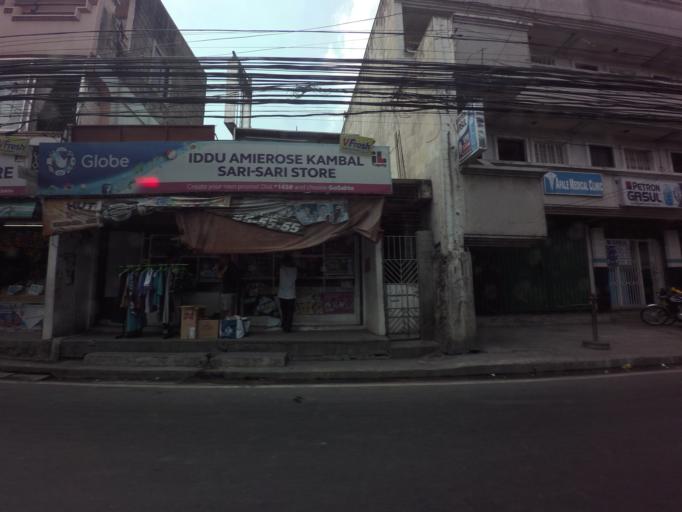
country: PH
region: Calabarzon
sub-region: Province of Rizal
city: Taguig
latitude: 14.5101
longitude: 121.0681
